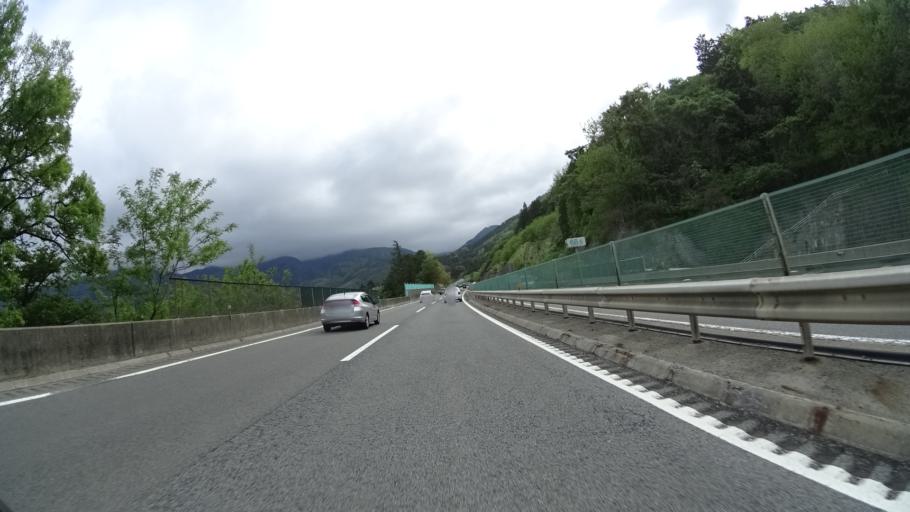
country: JP
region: Nagano
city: Nagano-shi
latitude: 36.5295
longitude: 138.0838
